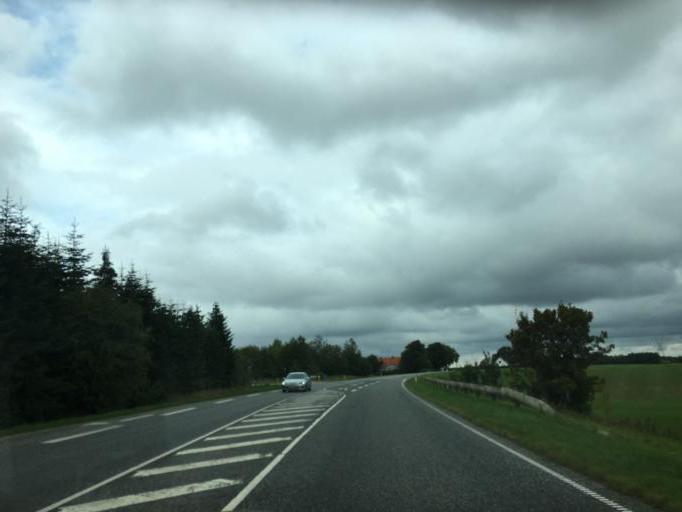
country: DK
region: South Denmark
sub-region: Kolding Kommune
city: Kolding
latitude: 55.5895
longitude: 9.4938
